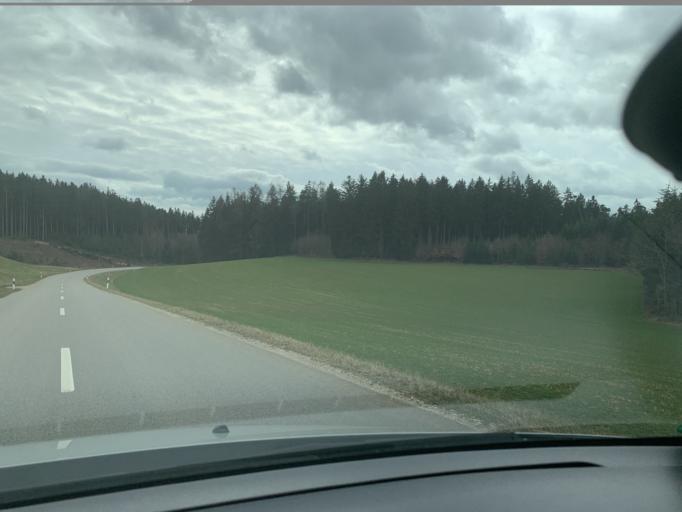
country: DE
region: Bavaria
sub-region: Lower Bavaria
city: Kumhausen
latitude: 48.5081
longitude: 12.2052
